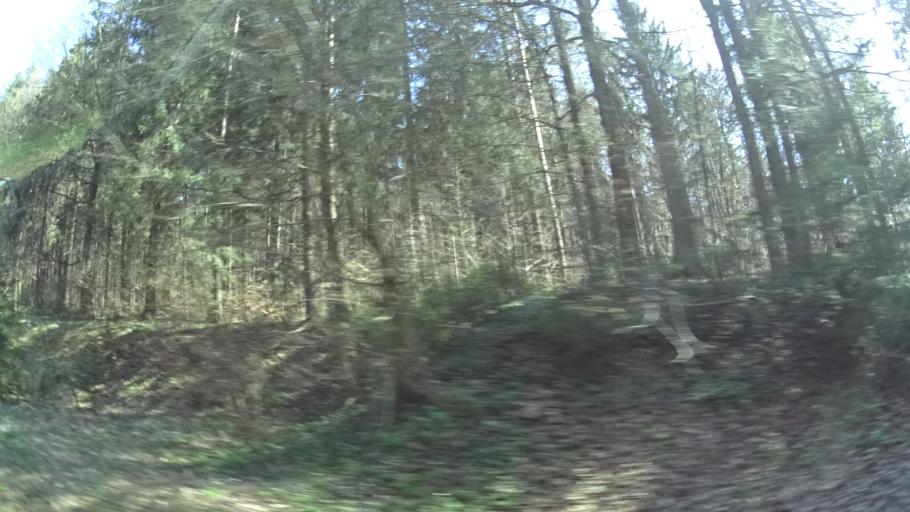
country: DE
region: Bavaria
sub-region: Upper Palatinate
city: Etzelwang
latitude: 49.4857
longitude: 11.6264
